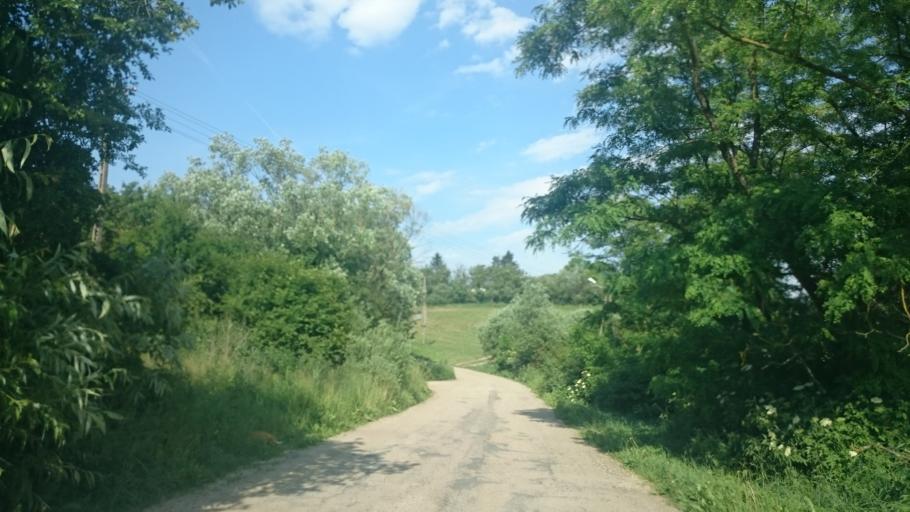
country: PL
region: Kujawsko-Pomorskie
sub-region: Powiat golubsko-dobrzynski
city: Radomin
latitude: 53.1225
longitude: 19.1376
